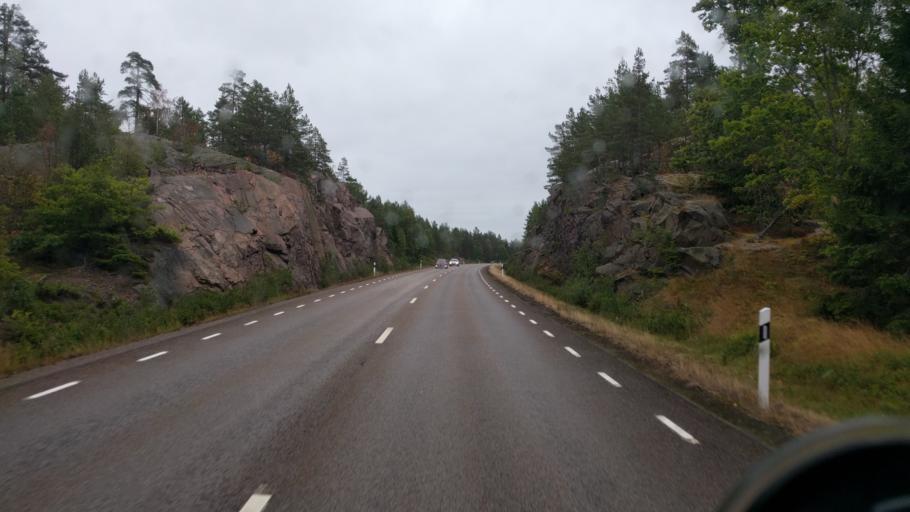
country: SE
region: Kalmar
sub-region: Vasterviks Kommun
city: Ankarsrum
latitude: 57.7047
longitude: 16.1981
